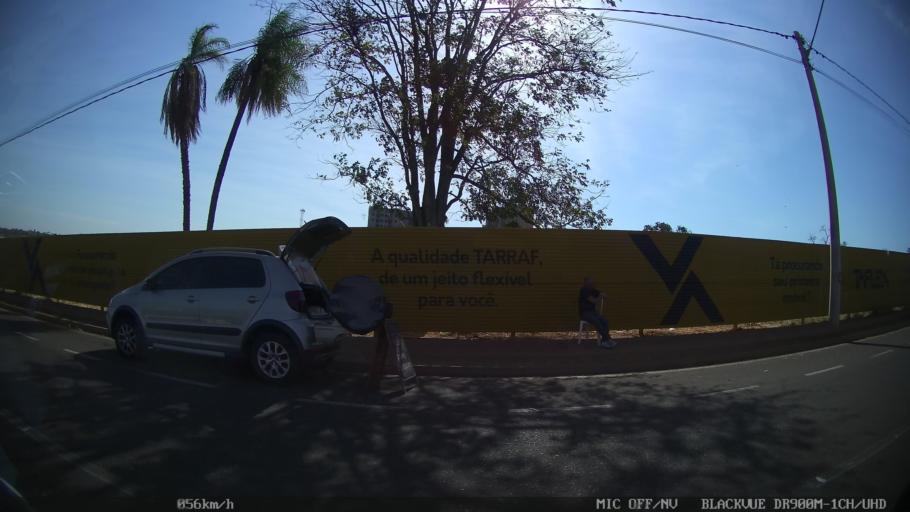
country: BR
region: Sao Paulo
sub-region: Sao Jose Do Rio Preto
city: Sao Jose do Rio Preto
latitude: -20.7916
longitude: -49.4226
